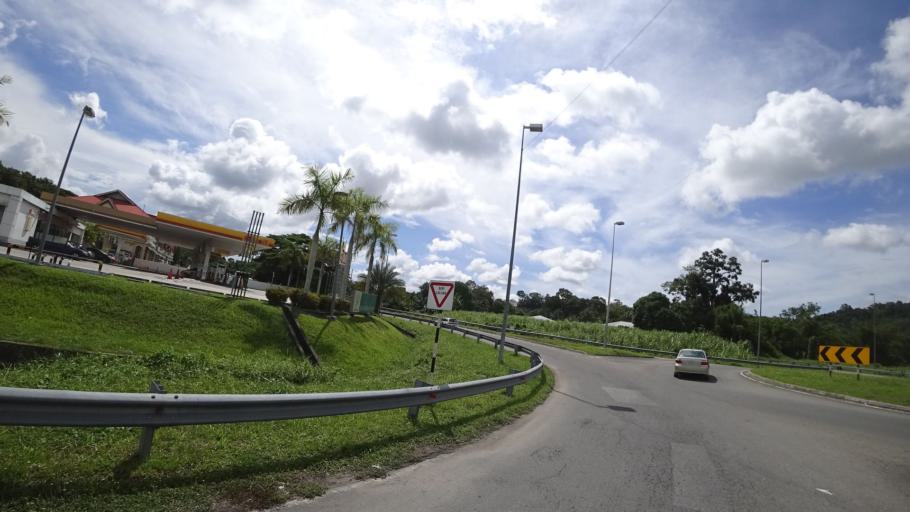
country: BN
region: Tutong
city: Tutong
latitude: 4.7680
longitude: 114.8235
